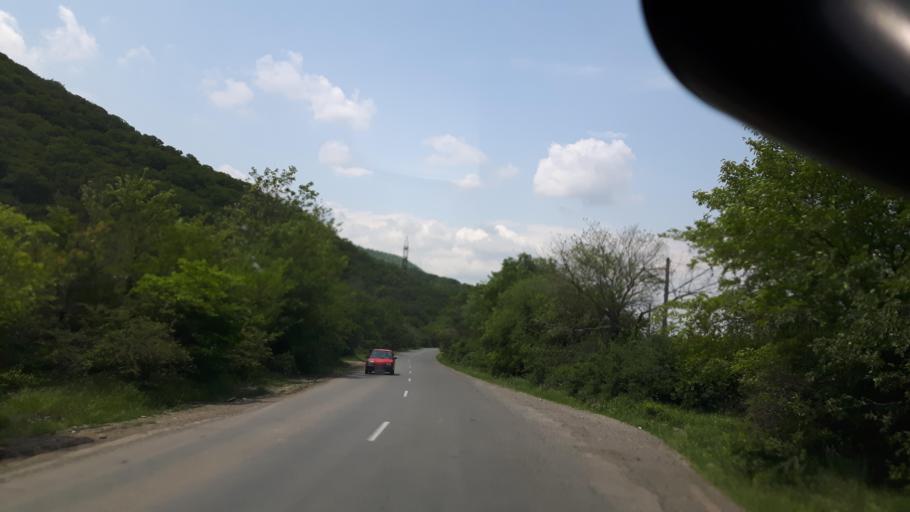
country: GE
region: Mtskheta-Mtianeti
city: Mtskheta
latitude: 41.8404
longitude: 44.6448
